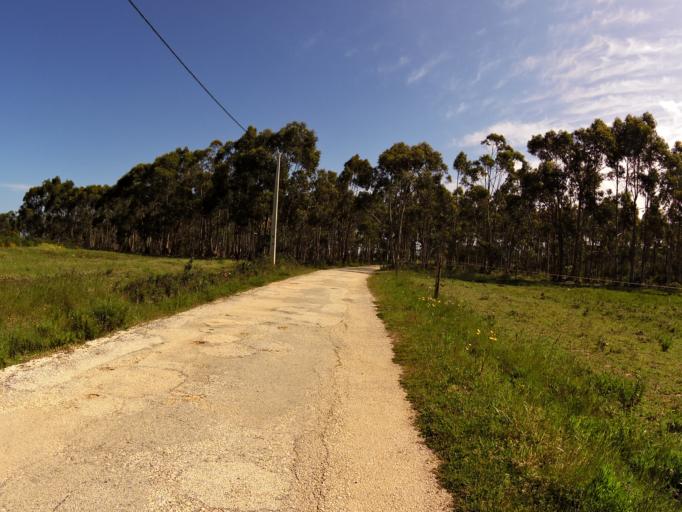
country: PT
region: Faro
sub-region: Aljezur
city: Aljezur
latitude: 37.3380
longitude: -8.8079
